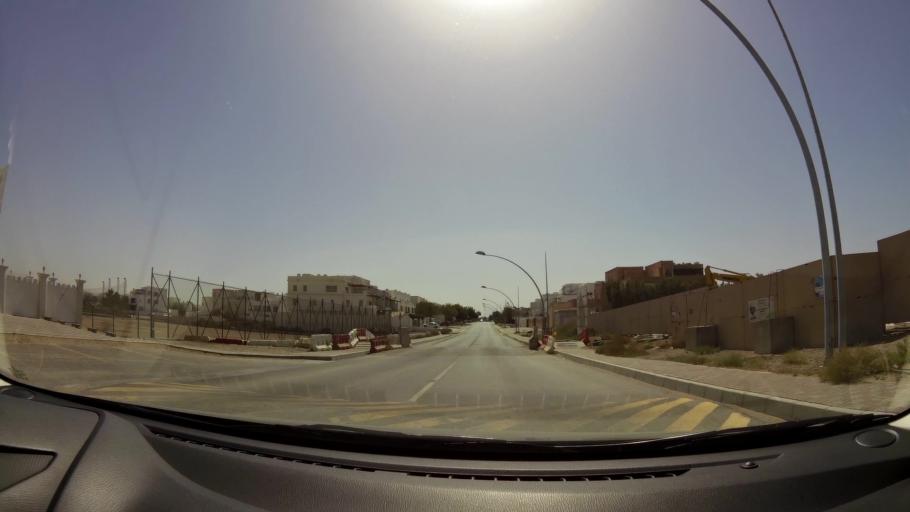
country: OM
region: Muhafazat Masqat
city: Bawshar
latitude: 23.6039
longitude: 58.3775
